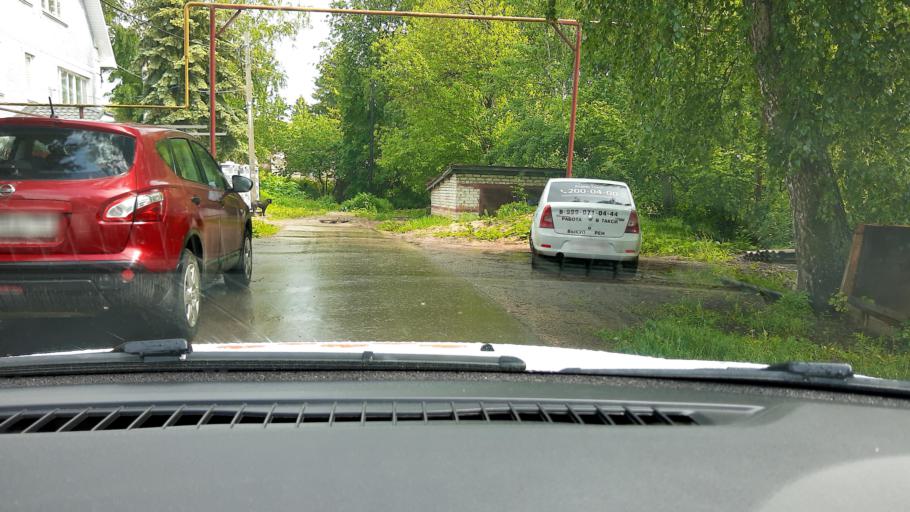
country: RU
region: Nizjnij Novgorod
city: Afonino
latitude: 56.2927
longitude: 44.0857
